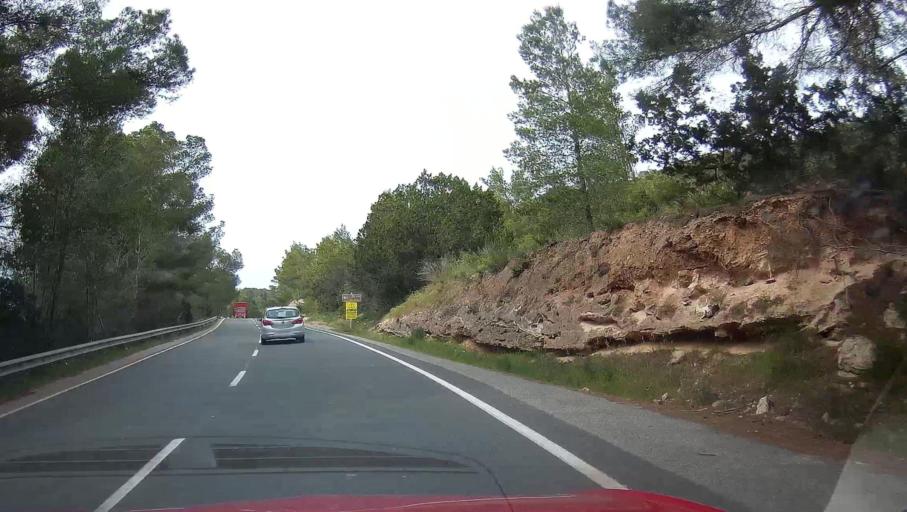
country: ES
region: Balearic Islands
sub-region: Illes Balears
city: Sant Joan de Labritja
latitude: 39.0996
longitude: 1.5114
